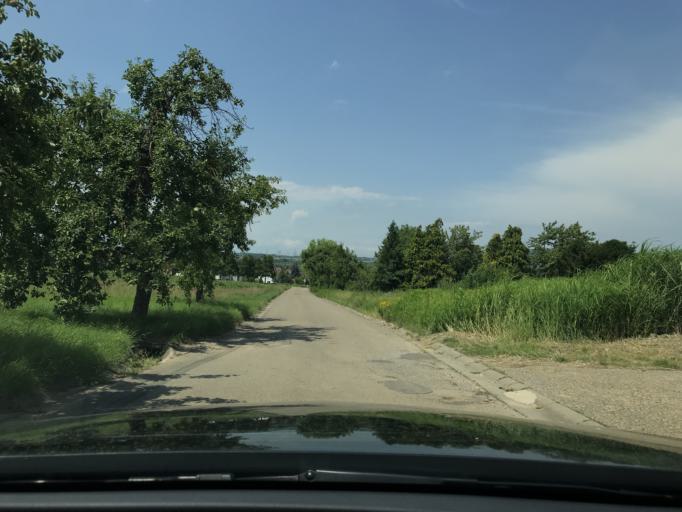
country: DE
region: Baden-Wuerttemberg
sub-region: Regierungsbezirk Stuttgart
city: Weinstadt-Endersbach
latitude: 48.8051
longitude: 9.3673
